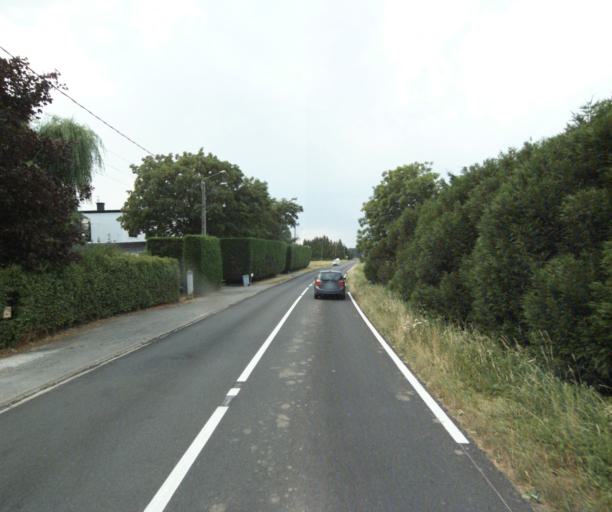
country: FR
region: Nord-Pas-de-Calais
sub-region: Departement du Nord
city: Quesnoy-sur-Deule
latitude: 50.7185
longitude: 2.9890
